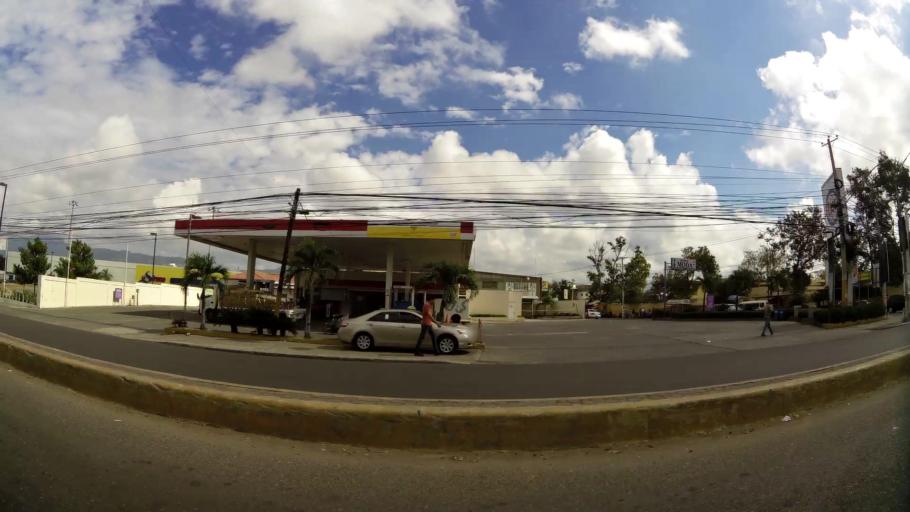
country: DO
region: Santiago
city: Santiago de los Caballeros
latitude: 19.4832
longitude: -70.7091
